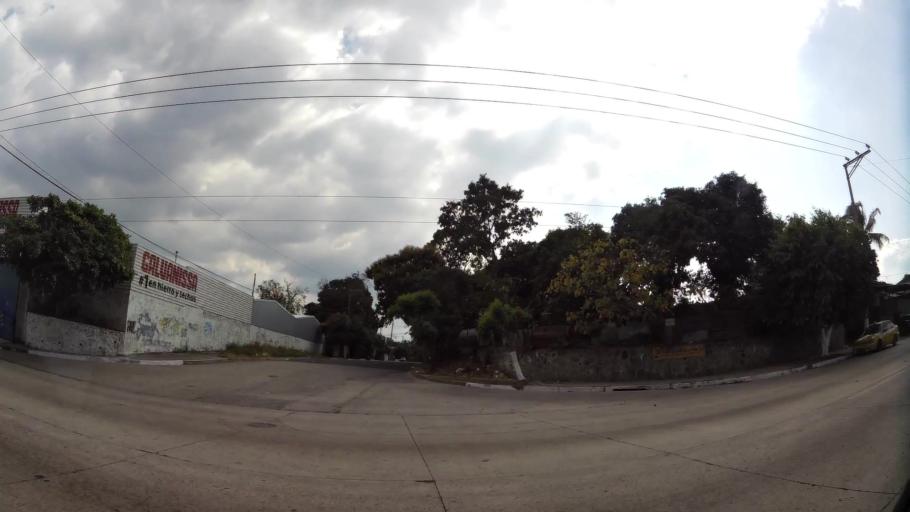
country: SV
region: San Salvador
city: Mejicanos
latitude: 13.7347
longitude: -89.2156
